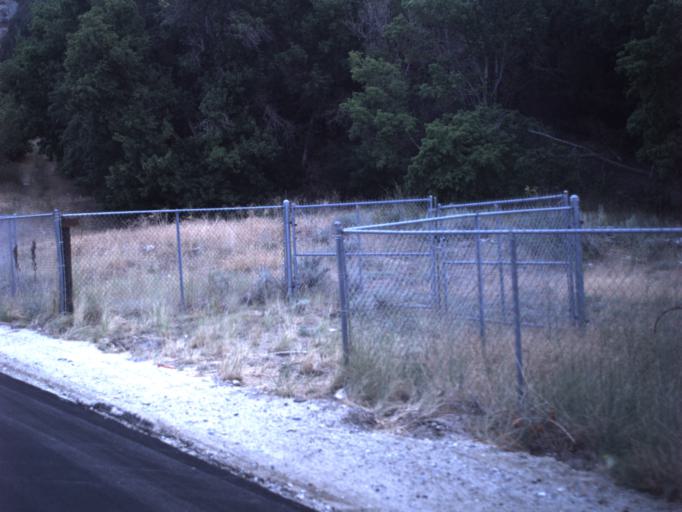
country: US
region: Utah
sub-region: Salt Lake County
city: Granite
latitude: 40.5735
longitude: -111.7859
